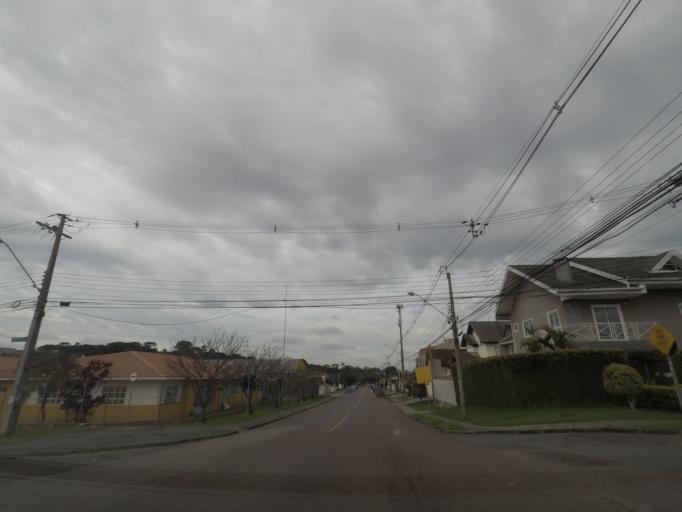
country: BR
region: Parana
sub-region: Pinhais
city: Pinhais
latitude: -25.4719
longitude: -49.2279
